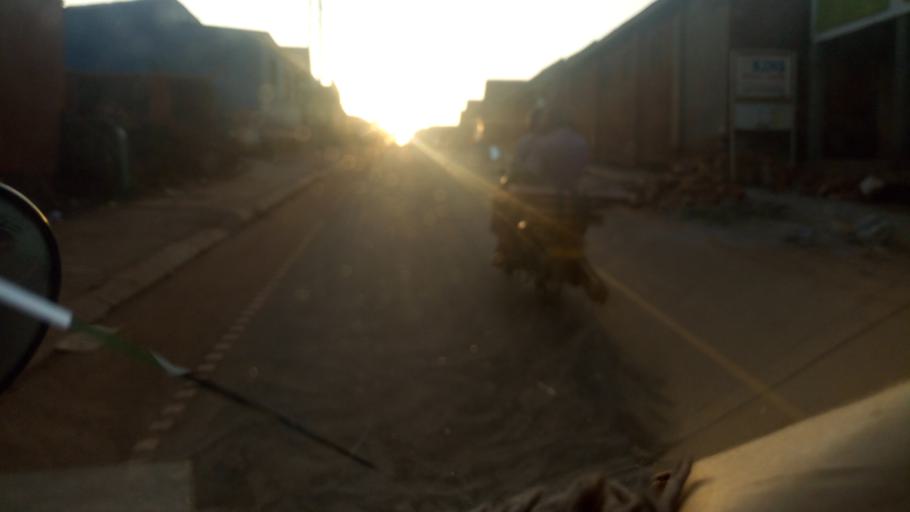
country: UG
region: Central Region
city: Kampala Central Division
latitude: 0.3609
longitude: 32.5567
